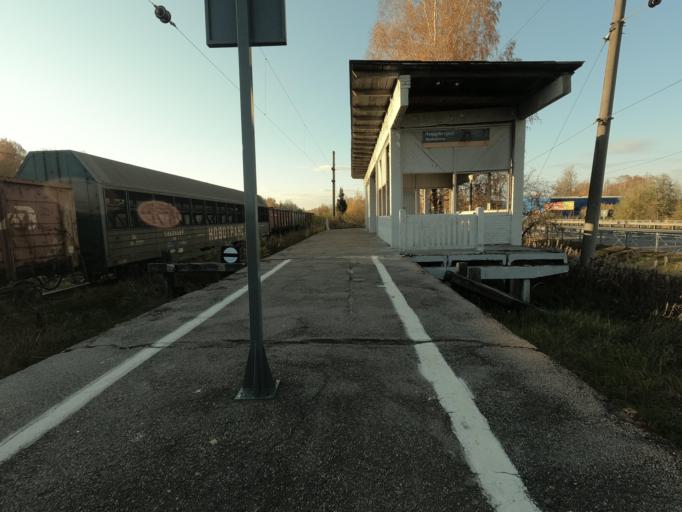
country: RU
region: Leningrad
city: Kirovsk
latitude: 59.8554
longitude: 31.0137
